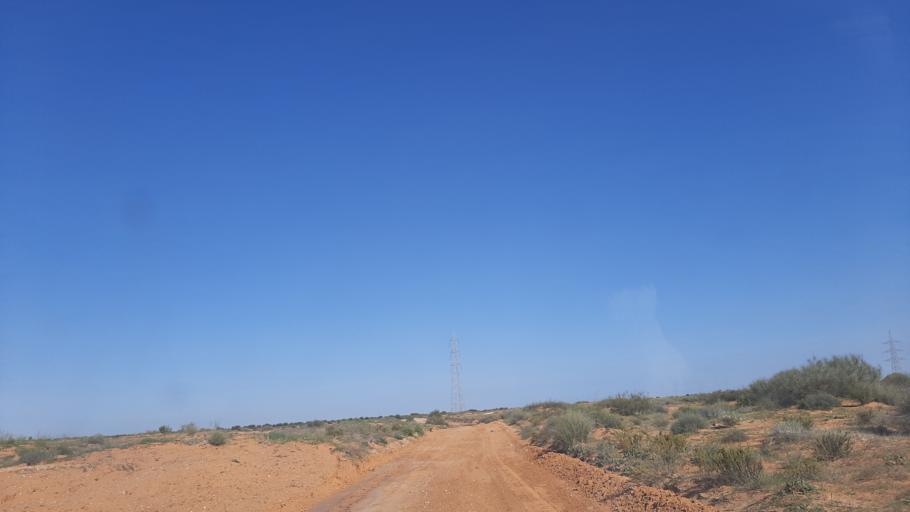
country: TN
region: Madanin
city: Medenine
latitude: 33.2769
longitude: 10.7729
